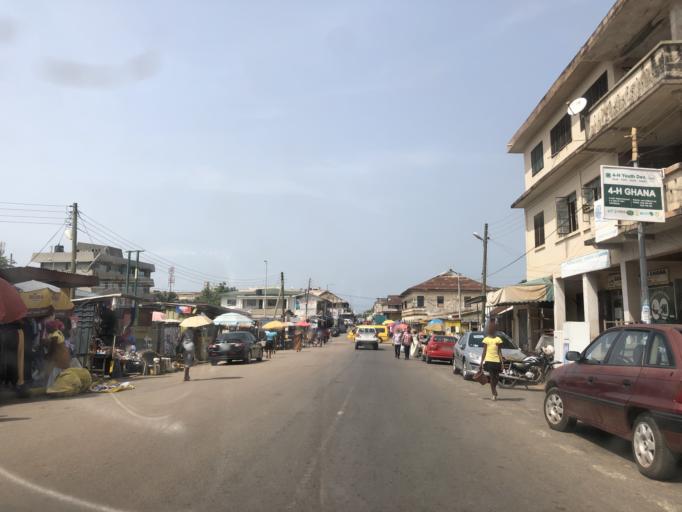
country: GH
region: Eastern
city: Koforidua
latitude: 6.0947
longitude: -0.2583
